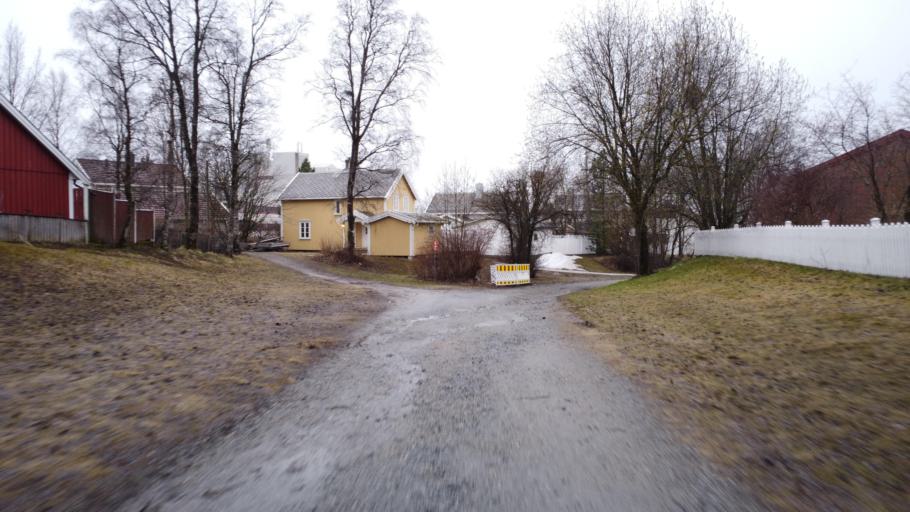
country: NO
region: Nordland
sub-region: Rana
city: Mo i Rana
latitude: 66.3121
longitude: 14.1423
